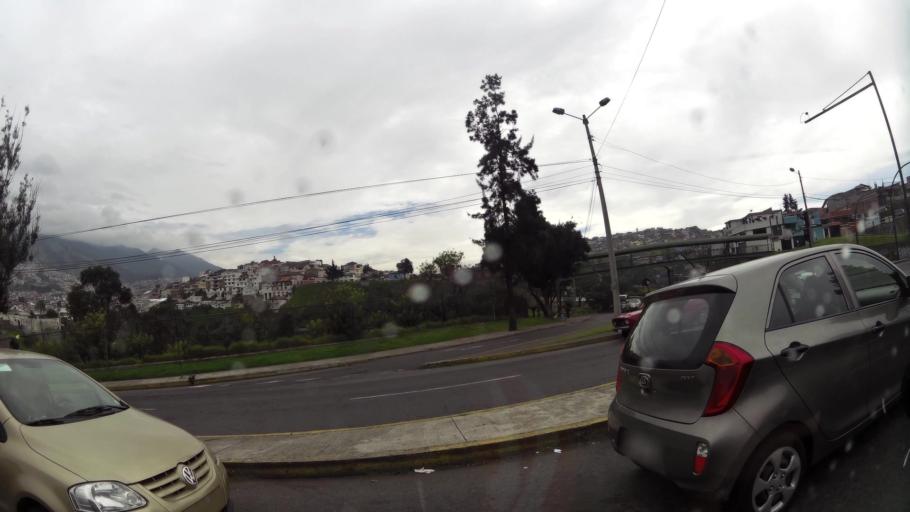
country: EC
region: Pichincha
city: Quito
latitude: -0.2329
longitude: -78.5090
